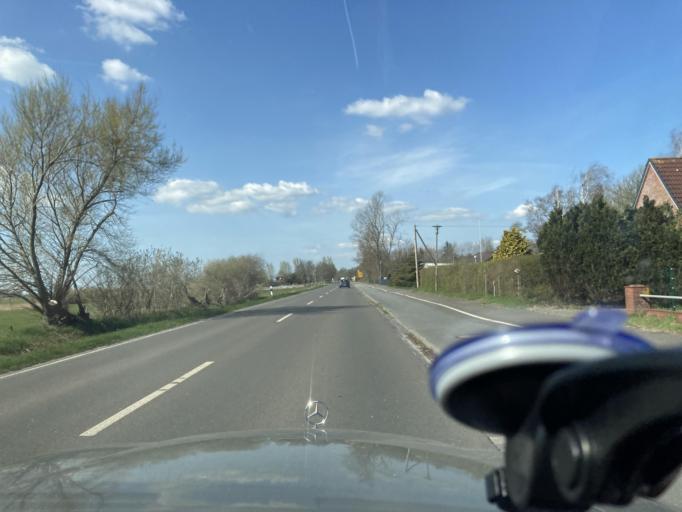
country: DE
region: Schleswig-Holstein
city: Krempel
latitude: 54.3047
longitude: 9.0361
